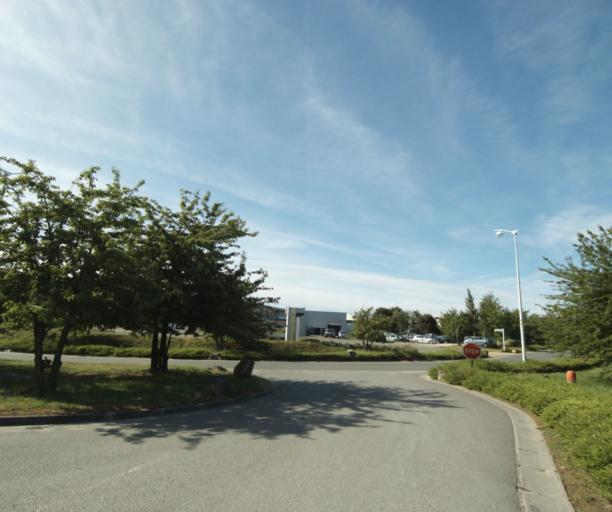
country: FR
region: Centre
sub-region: Departement d'Eure-et-Loir
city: Luce
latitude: 48.4219
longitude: 1.4490
